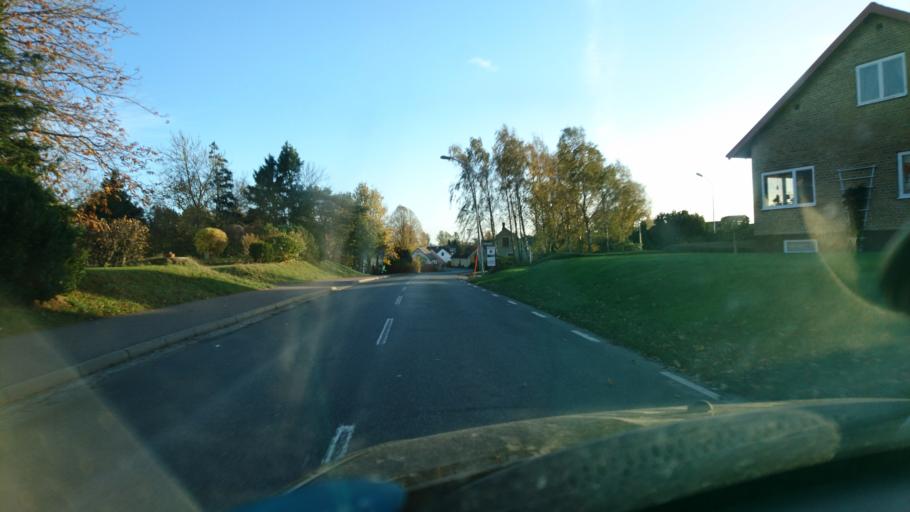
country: SE
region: Skane
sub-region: Tomelilla Kommun
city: Tomelilla
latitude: 55.5534
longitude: 14.1148
